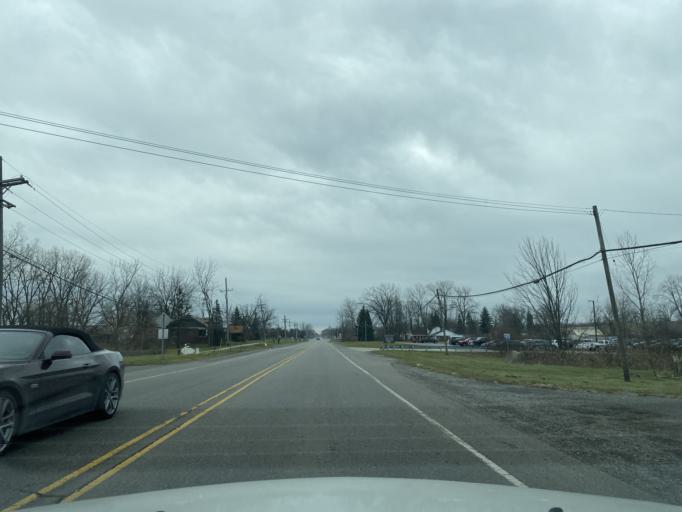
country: US
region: Michigan
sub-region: Wayne County
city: Taylor
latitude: 42.2154
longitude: -83.2879
